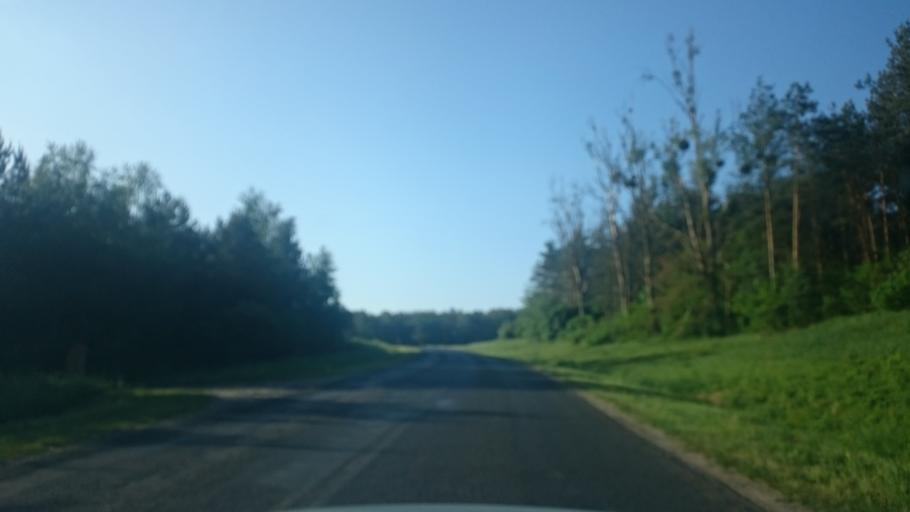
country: PL
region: Kujawsko-Pomorskie
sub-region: Powiat golubsko-dobrzynski
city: Golub-Dobrzyn
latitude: 53.0909
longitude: 19.0497
